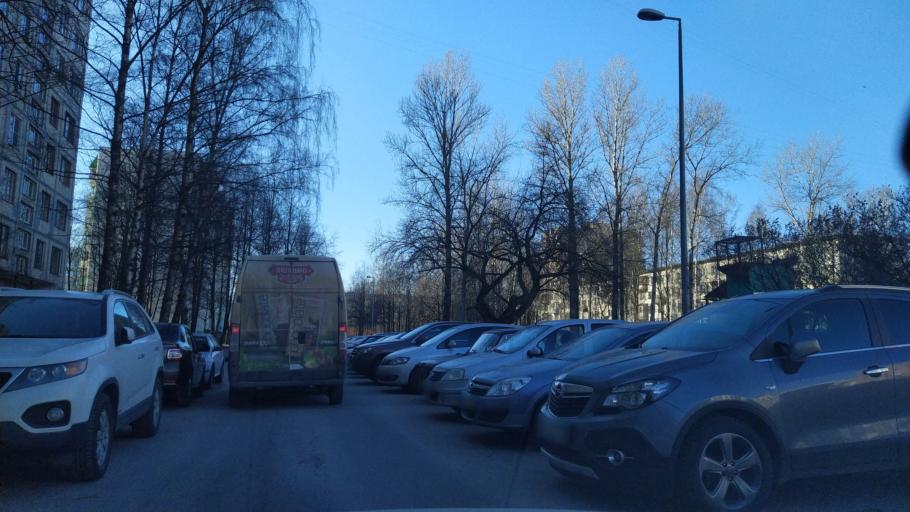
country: RU
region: Leningrad
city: Akademicheskoe
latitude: 60.0161
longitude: 30.4067
